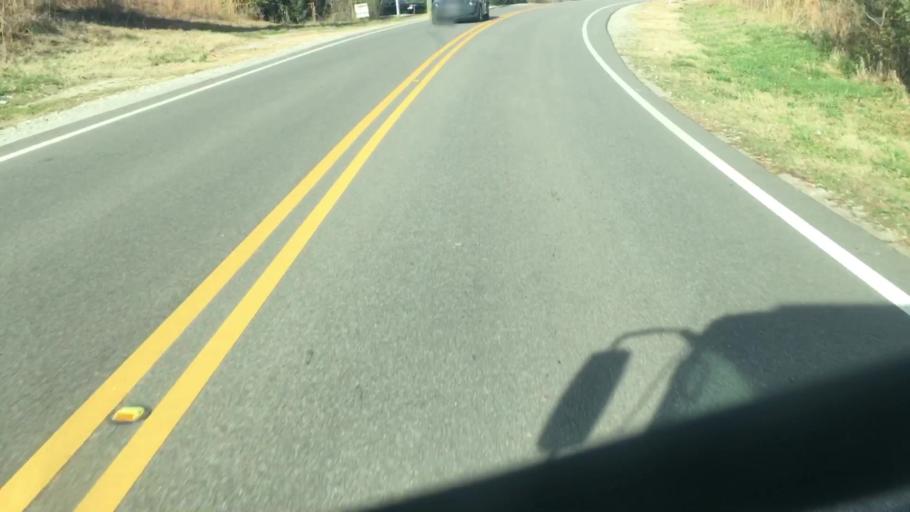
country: US
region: Alabama
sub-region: Shelby County
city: Brook Highland
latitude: 33.4787
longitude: -86.6690
